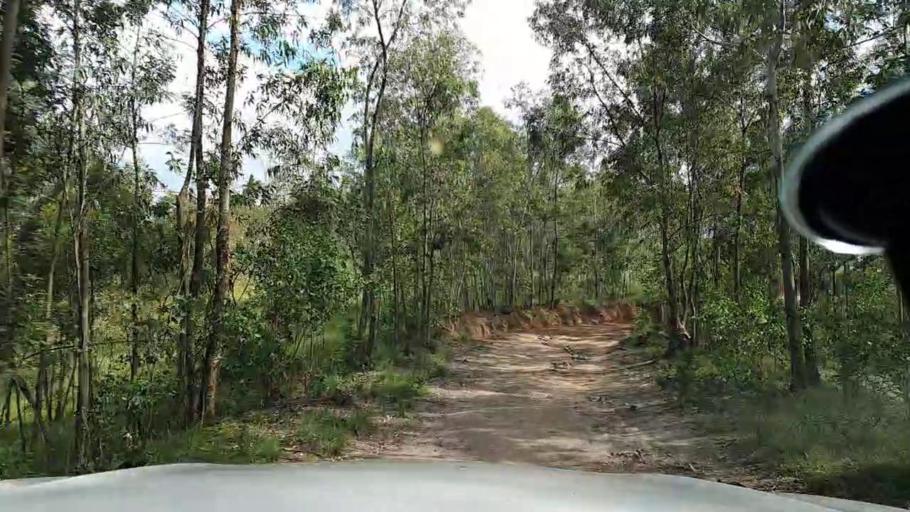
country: RW
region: Kigali
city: Kigali
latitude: -1.7830
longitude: 29.8377
